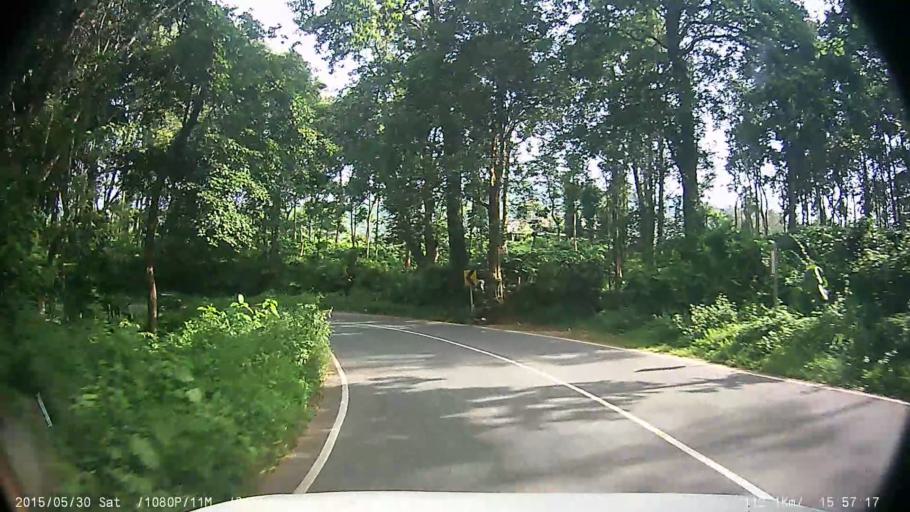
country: IN
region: Kerala
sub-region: Wayanad
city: Kalpetta
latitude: 11.6552
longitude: 76.0868
